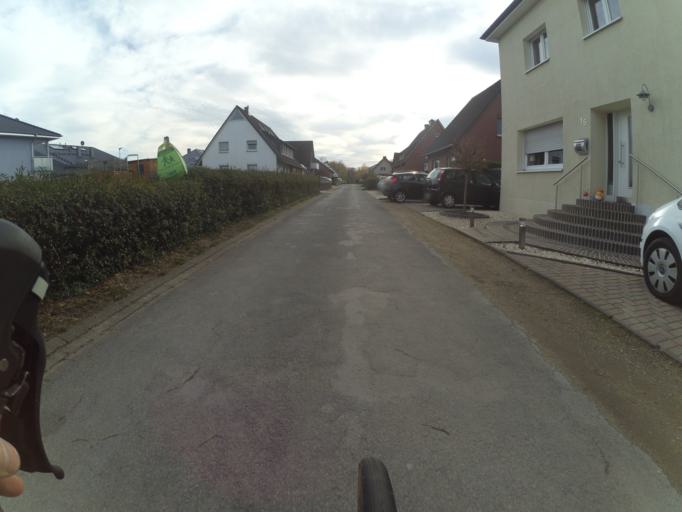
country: DE
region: North Rhine-Westphalia
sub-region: Regierungsbezirk Munster
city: Tecklenburg
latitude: 52.2643
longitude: 7.7912
